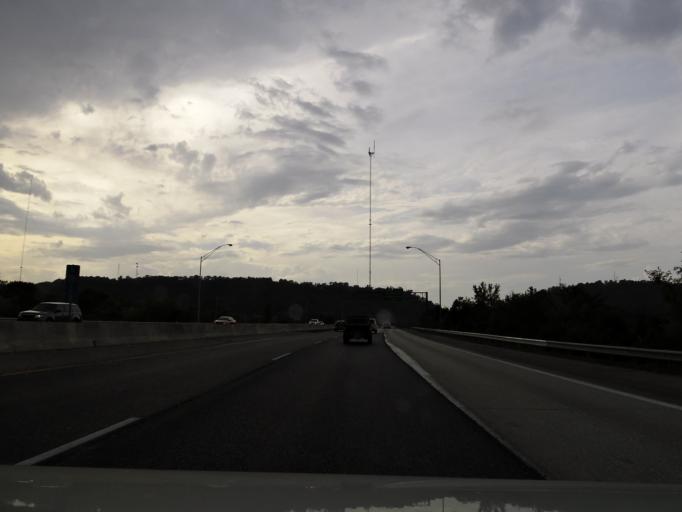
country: US
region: Tennessee
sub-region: Knox County
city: Knoxville
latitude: 35.9851
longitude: -83.9482
